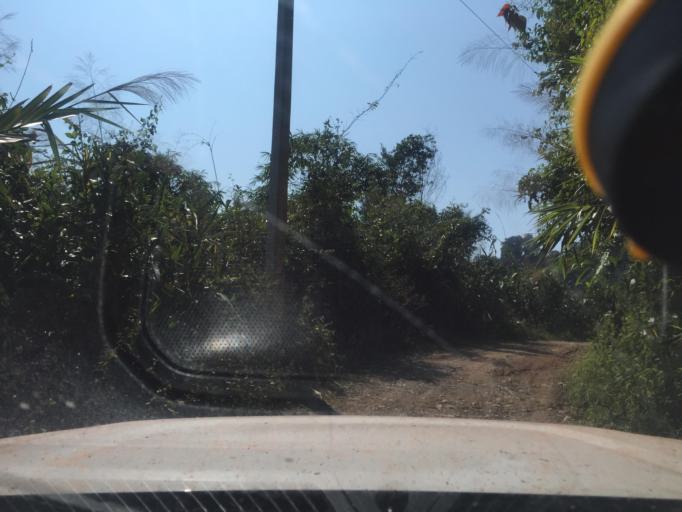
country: LA
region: Phongsali
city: Phongsali
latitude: 21.6570
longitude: 102.4174
